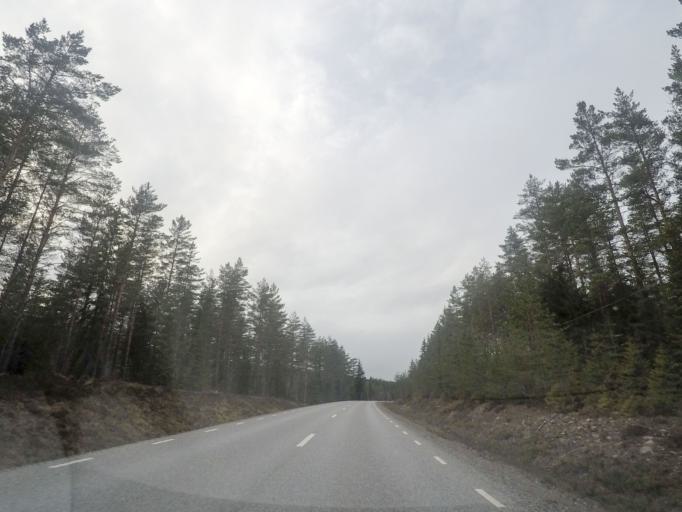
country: SE
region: OErebro
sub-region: Ljusnarsbergs Kommun
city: Kopparberg
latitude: 59.8944
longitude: 15.1047
